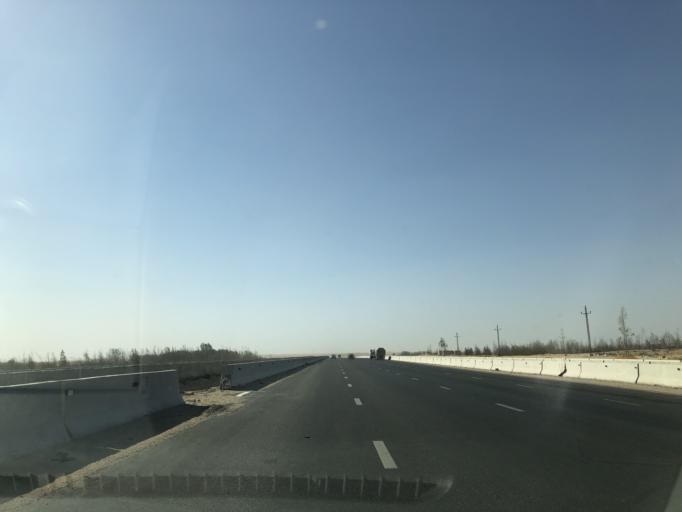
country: EG
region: Al Jizah
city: Madinat Sittah Uktubar
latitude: 29.9863
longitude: 30.8595
